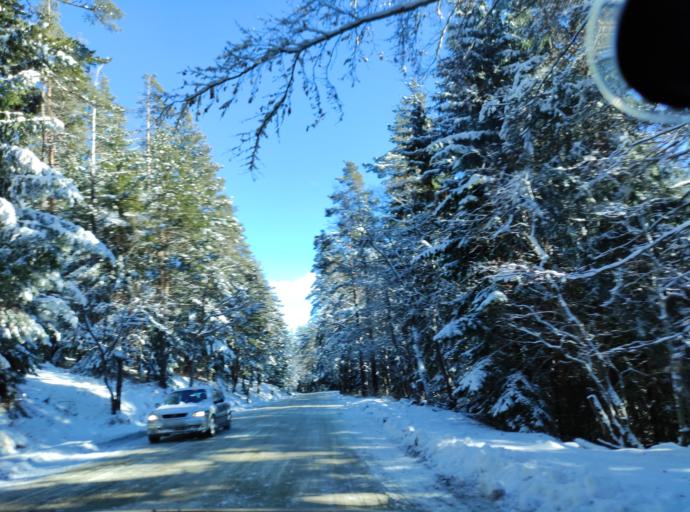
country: BG
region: Sofia-Capital
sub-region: Stolichna Obshtina
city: Sofia
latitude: 42.5890
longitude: 23.2995
